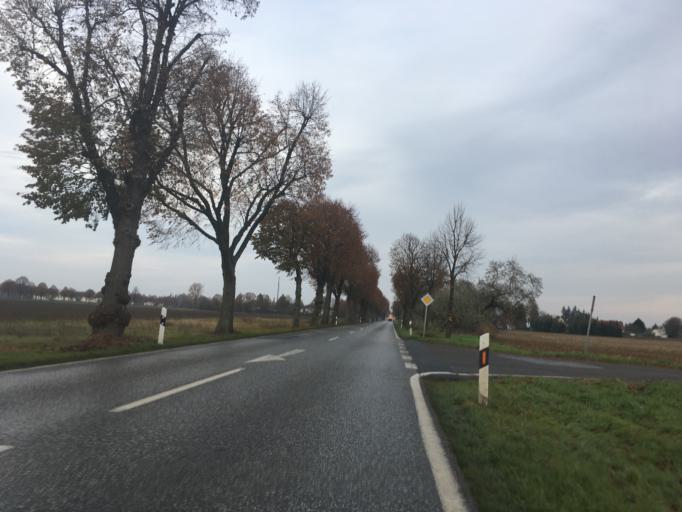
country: DE
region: Brandenburg
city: Letschin
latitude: 52.6342
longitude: 14.3558
